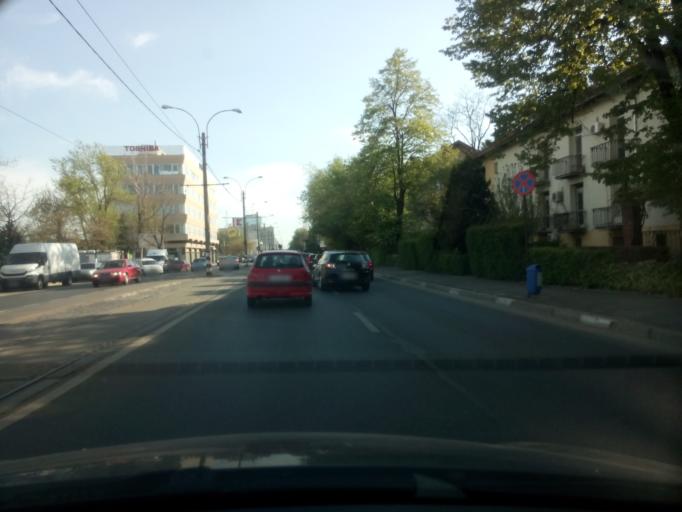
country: RO
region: Bucuresti
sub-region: Municipiul Bucuresti
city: Bucharest
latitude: 44.4663
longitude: 26.1086
